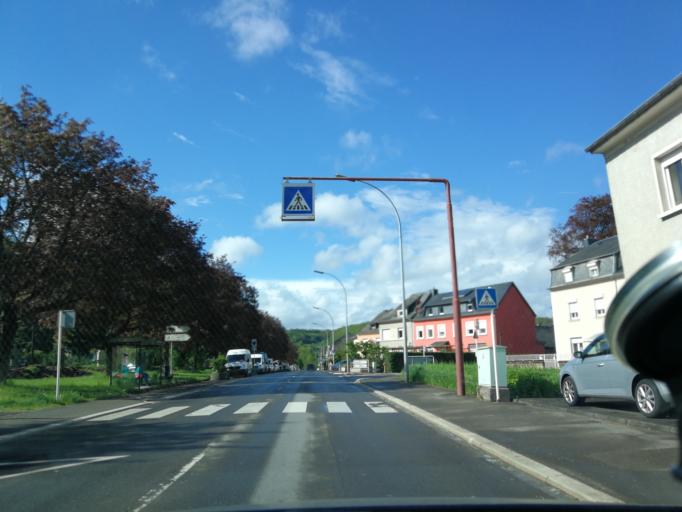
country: DE
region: Rheinland-Pfalz
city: Oberbillig
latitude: 49.7172
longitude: 6.5000
